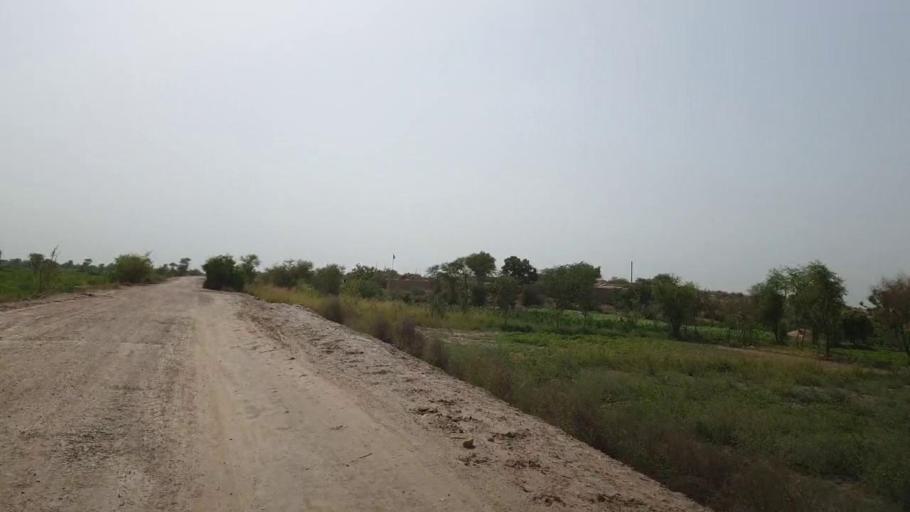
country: PK
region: Sindh
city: Bandhi
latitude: 26.5386
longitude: 68.3904
